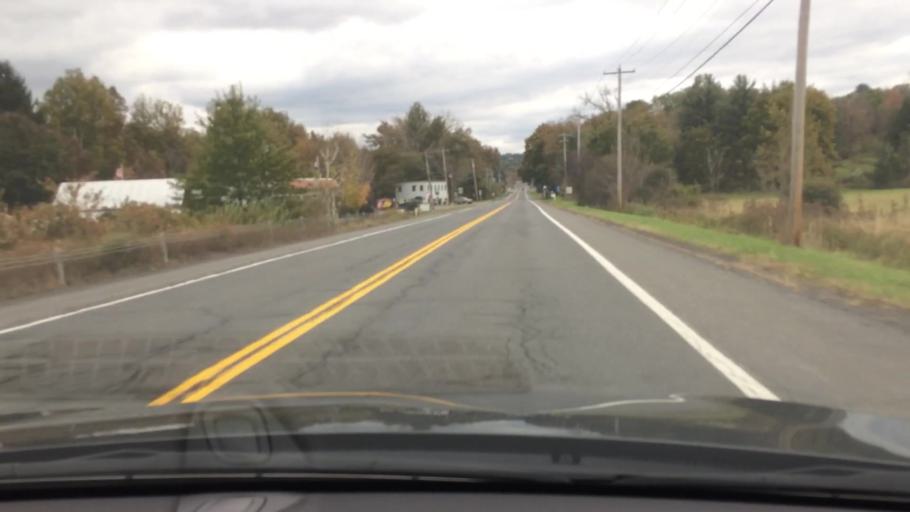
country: US
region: New York
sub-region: Columbia County
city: Oakdale
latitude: 42.1243
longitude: -73.7234
